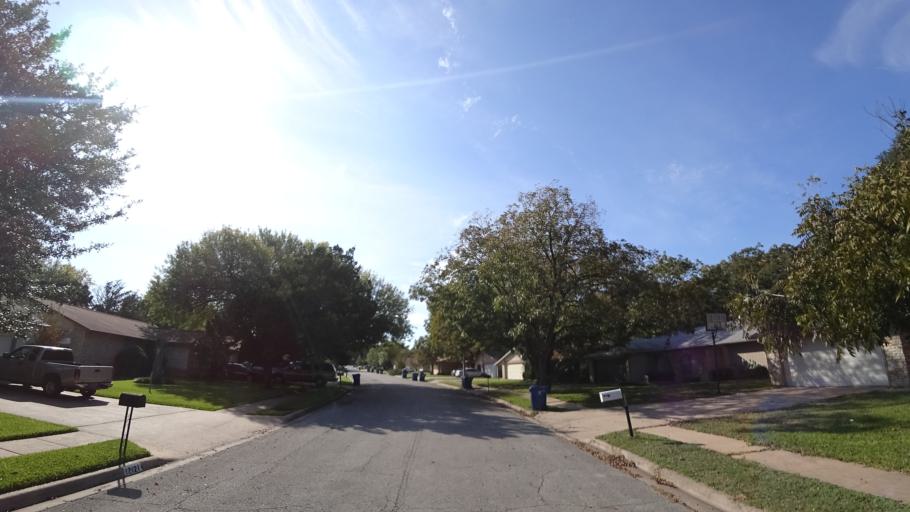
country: US
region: Texas
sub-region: Williamson County
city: Anderson Mill
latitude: 30.4525
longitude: -97.8002
